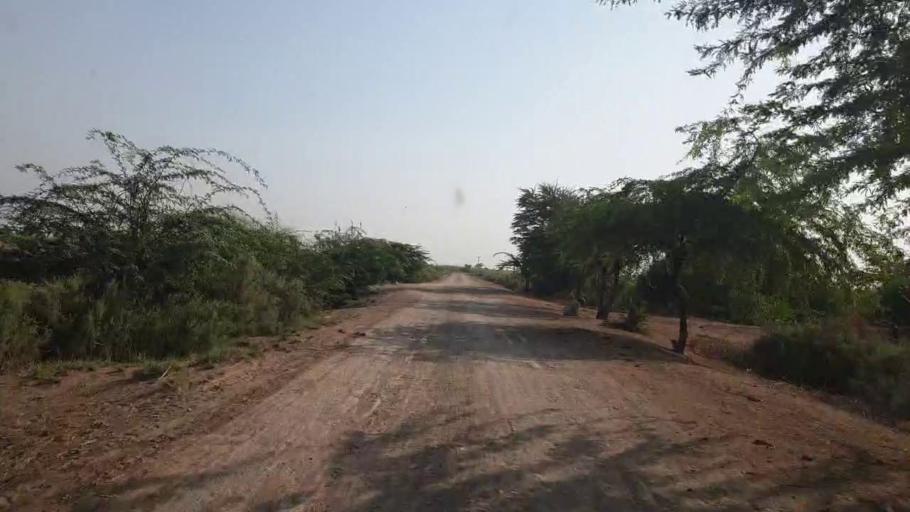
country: PK
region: Sindh
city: Sanghar
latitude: 26.0436
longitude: 68.8975
